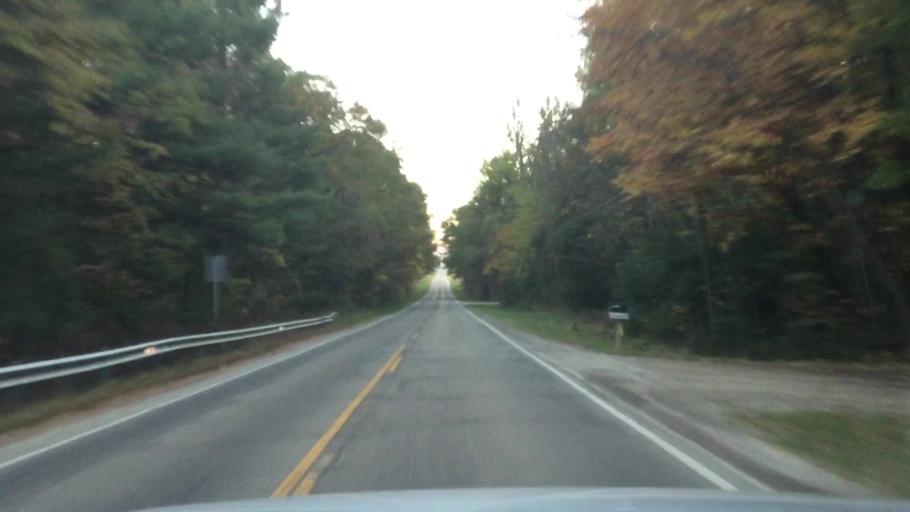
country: US
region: Michigan
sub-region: Lapeer County
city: Barnes Lake-Millers Lake
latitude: 43.1204
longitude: -83.2503
